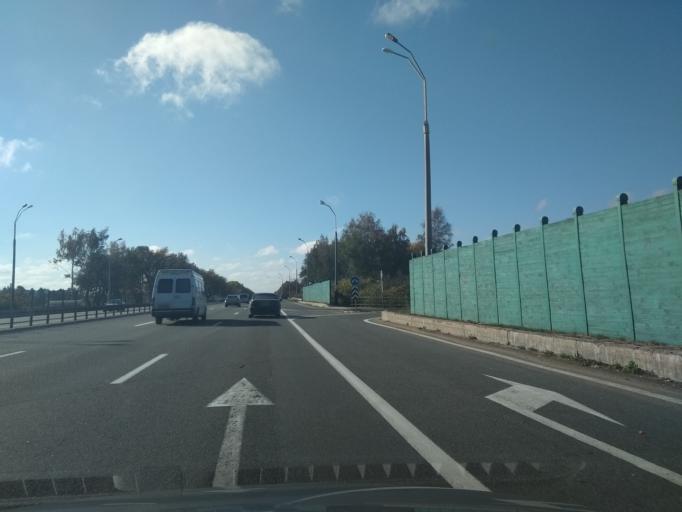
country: BY
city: Fanipol
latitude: 53.7623
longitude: 27.3386
